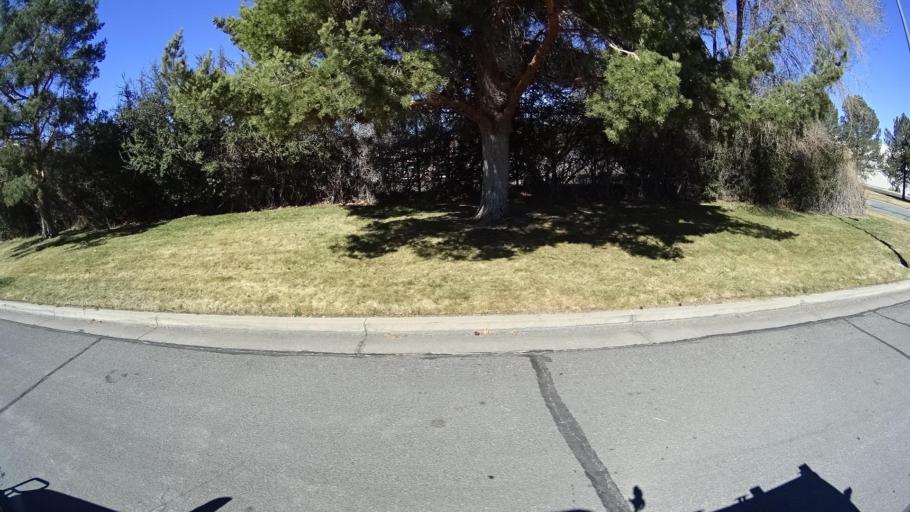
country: US
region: Nevada
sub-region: Washoe County
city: Sparks
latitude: 39.4849
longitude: -119.7620
